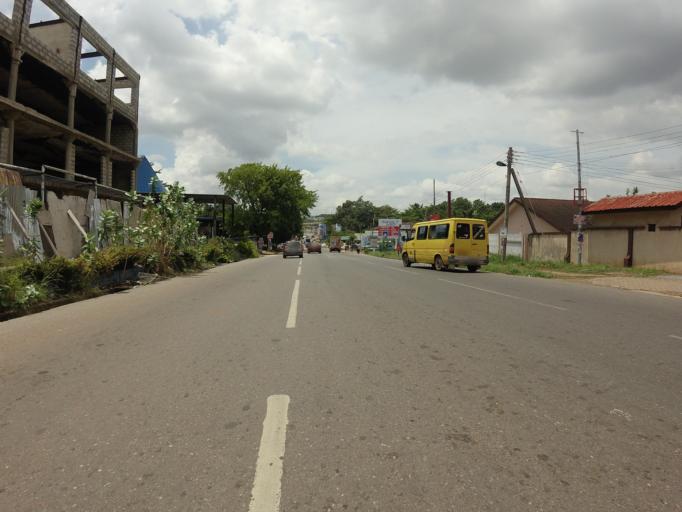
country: GH
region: Greater Accra
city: Medina Estates
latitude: 5.6298
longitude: -0.1738
